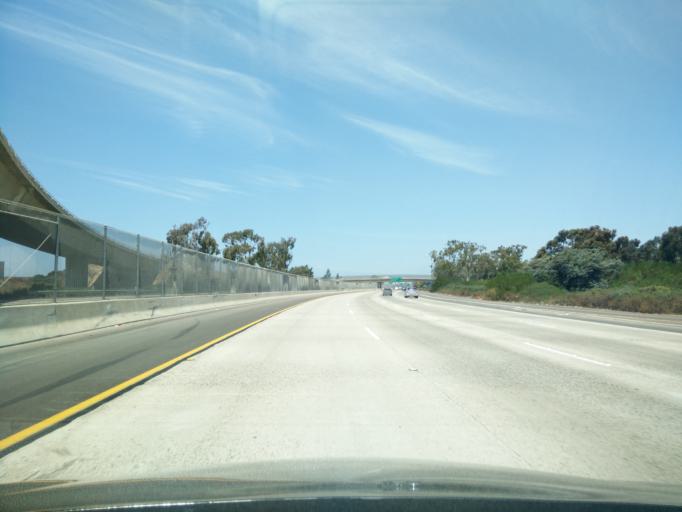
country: US
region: California
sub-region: San Diego County
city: Imperial Beach
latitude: 32.5658
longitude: -117.0740
